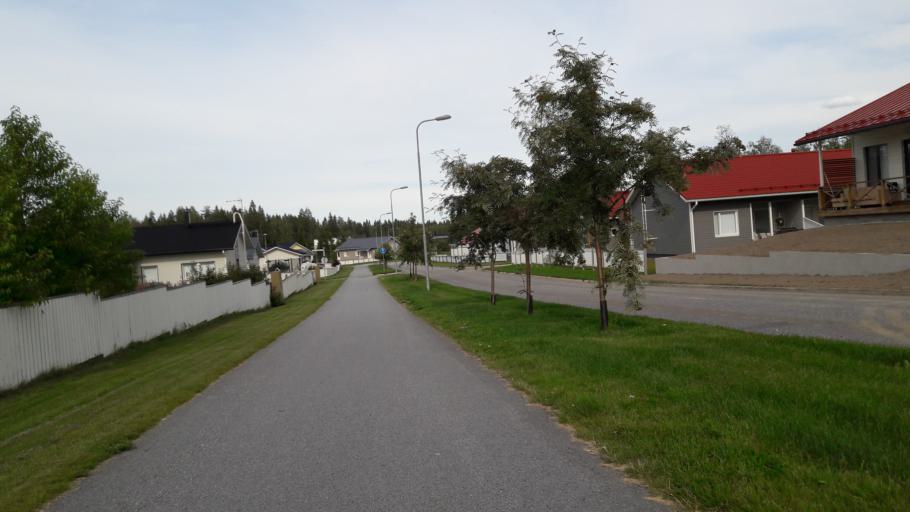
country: FI
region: North Karelia
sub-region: Joensuu
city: Joensuu
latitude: 62.5715
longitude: 29.8227
